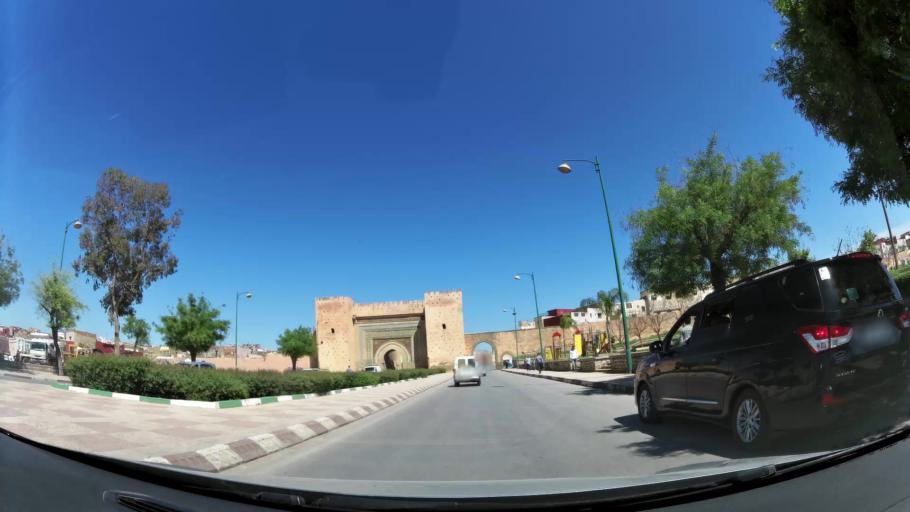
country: MA
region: Meknes-Tafilalet
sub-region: Meknes
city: Meknes
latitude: 33.8915
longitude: -5.5738
